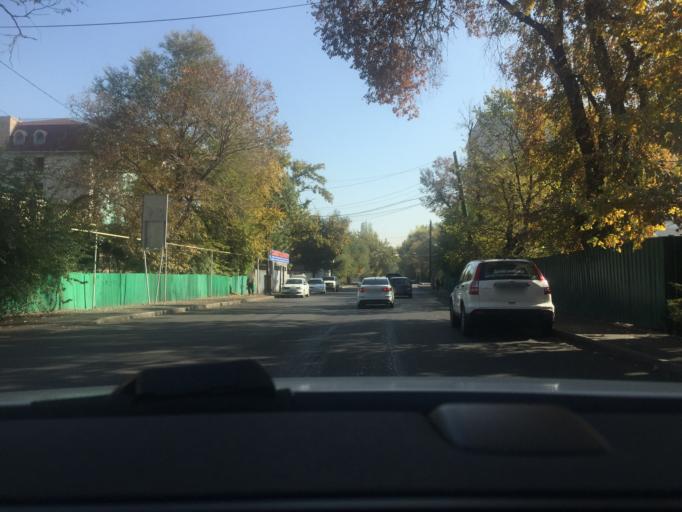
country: KZ
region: Almaty Qalasy
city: Almaty
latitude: 43.2493
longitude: 76.9154
